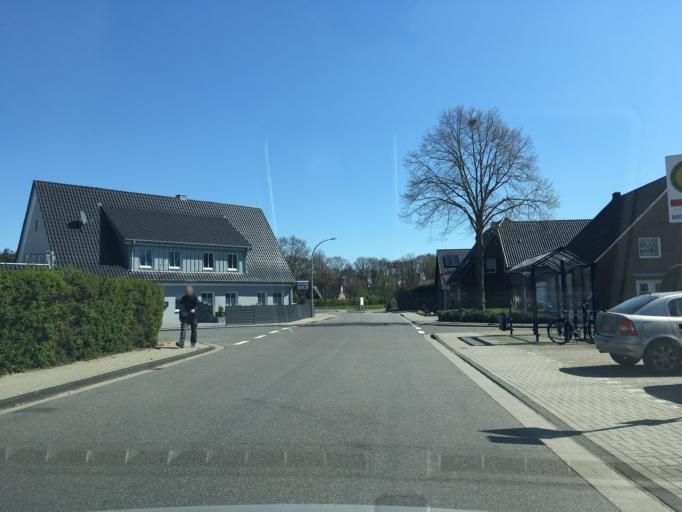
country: DE
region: North Rhine-Westphalia
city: Stadtlohn
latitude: 51.9984
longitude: 6.8813
